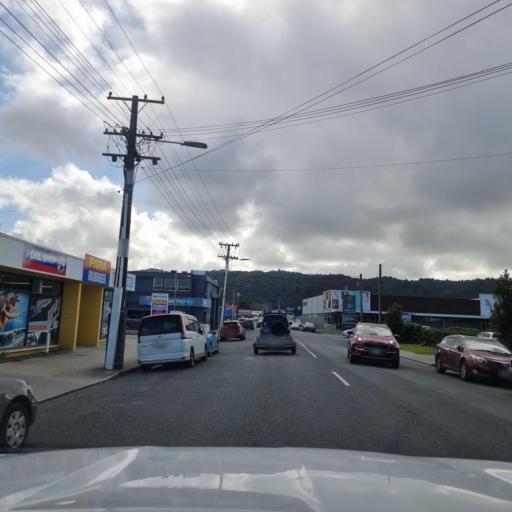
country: NZ
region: Northland
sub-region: Whangarei
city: Whangarei
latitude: -35.7312
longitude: 174.3199
